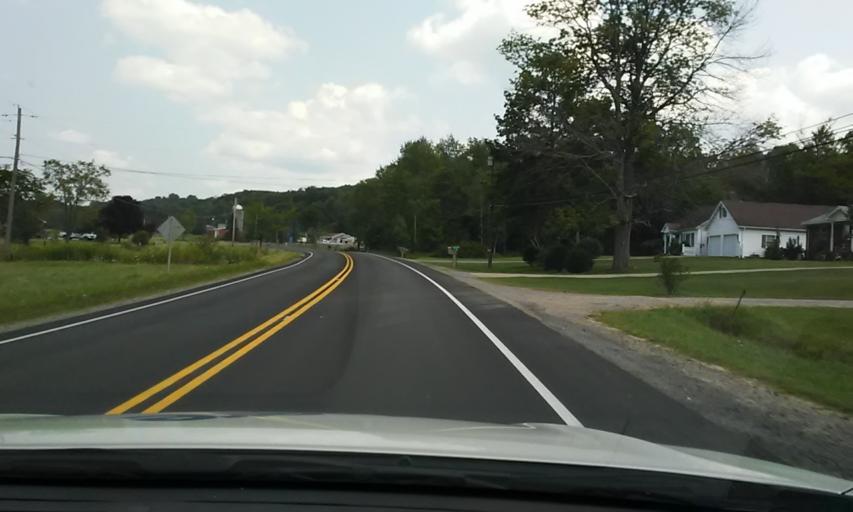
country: US
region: Pennsylvania
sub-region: Elk County
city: Saint Marys
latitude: 41.4426
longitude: -78.4803
